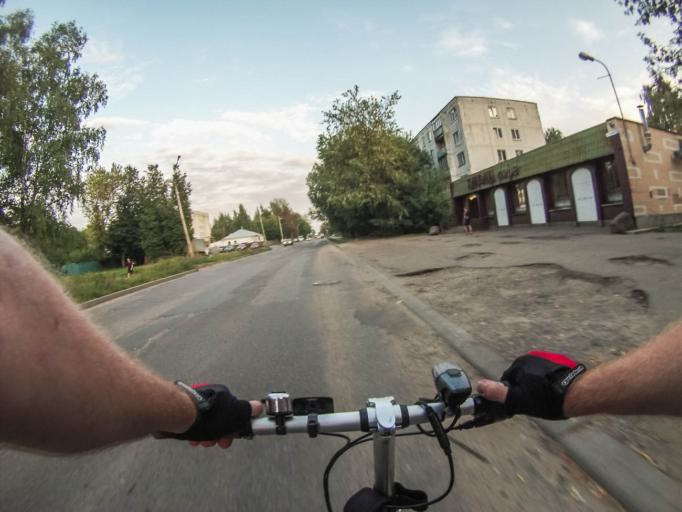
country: RU
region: Kostroma
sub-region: Kostromskoy Rayon
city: Kostroma
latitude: 57.7792
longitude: 40.9529
